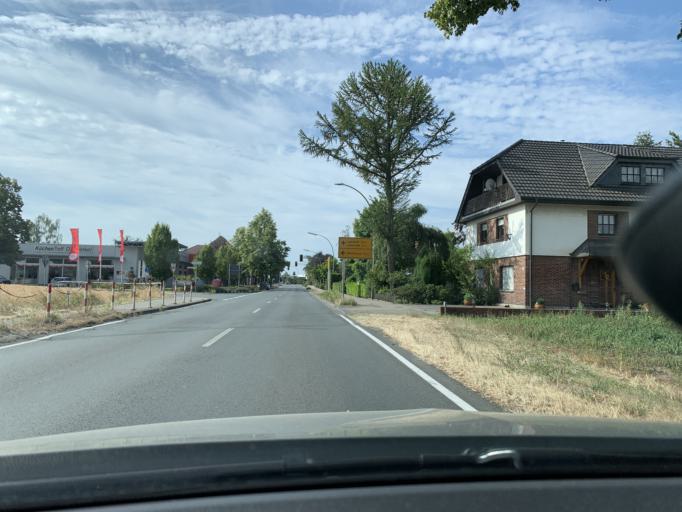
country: DE
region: North Rhine-Westphalia
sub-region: Regierungsbezirk Detmold
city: Langenberg
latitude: 51.7445
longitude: 8.3811
